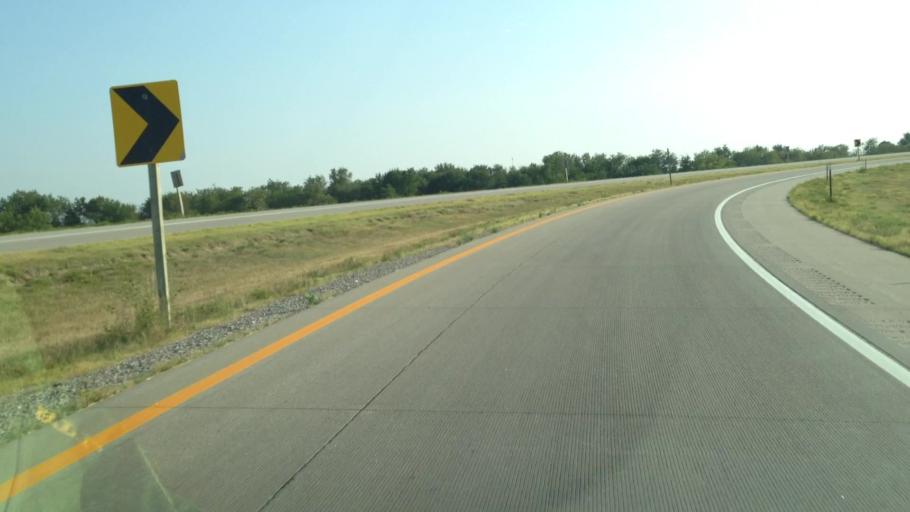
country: US
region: Kansas
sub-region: Franklin County
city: Ottawa
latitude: 38.6358
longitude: -95.2166
